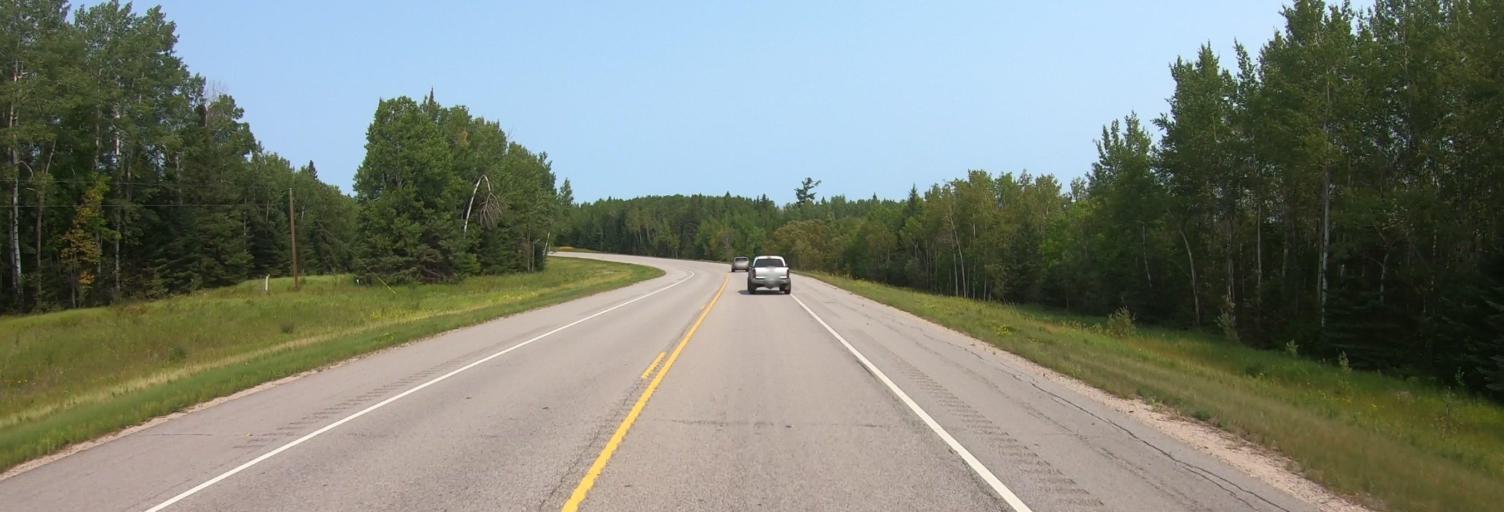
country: CA
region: Ontario
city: Fort Frances
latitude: 48.3626
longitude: -92.9632
